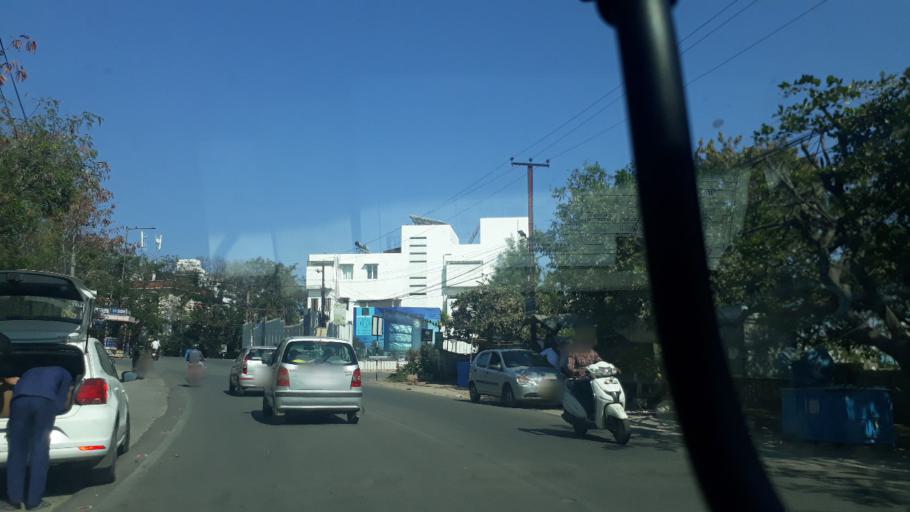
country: IN
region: Telangana
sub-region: Hyderabad
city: Hyderabad
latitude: 17.4181
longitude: 78.4003
